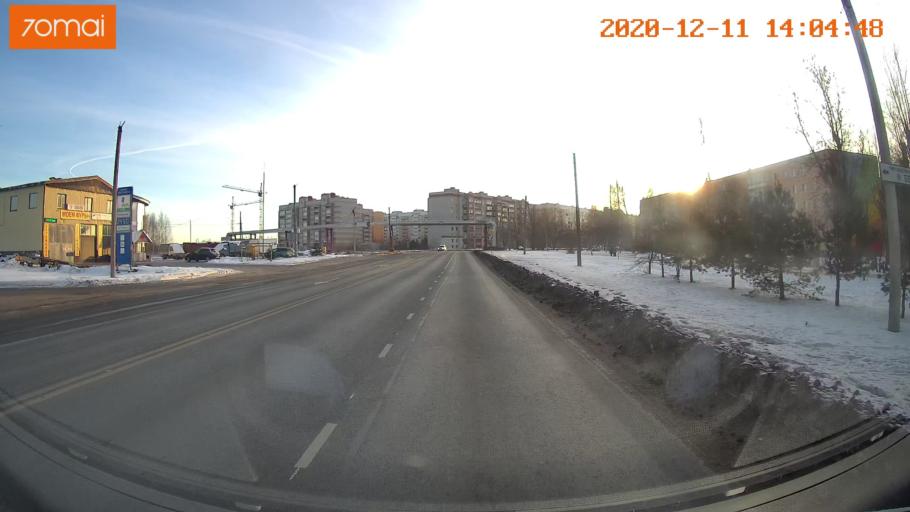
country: RU
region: Kostroma
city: Oktyabr'skiy
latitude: 57.7517
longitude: 41.0163
